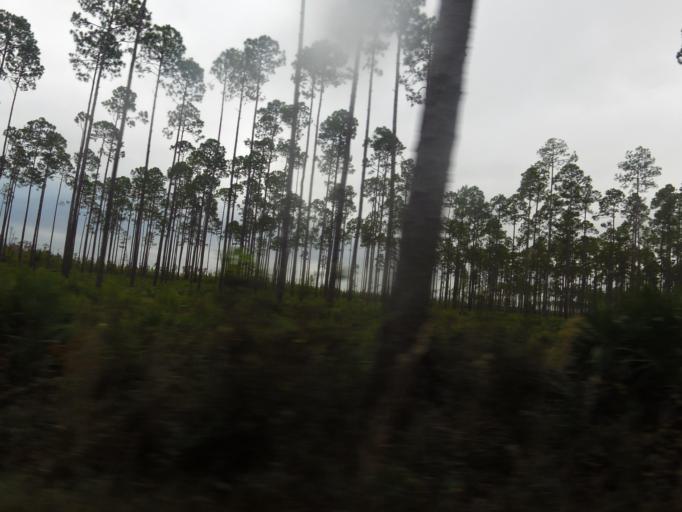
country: US
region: Georgia
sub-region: Charlton County
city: Folkston
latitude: 30.7085
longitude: -82.1584
